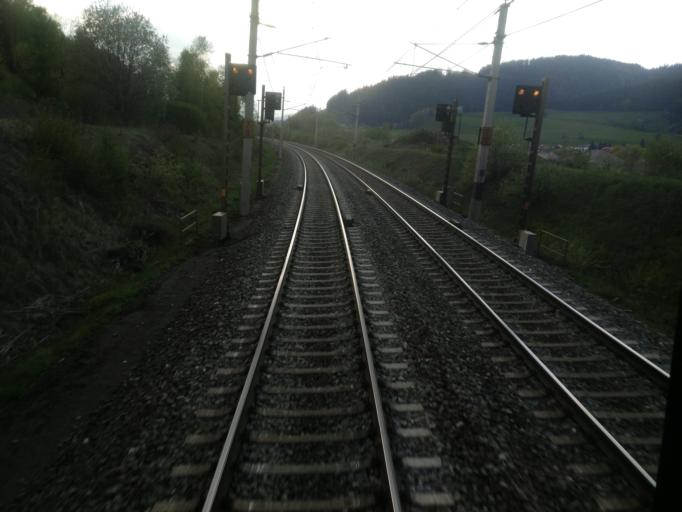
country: AT
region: Styria
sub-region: Politischer Bezirk Bruck-Muerzzuschlag
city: Oberaich
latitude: 47.4085
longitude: 15.2035
